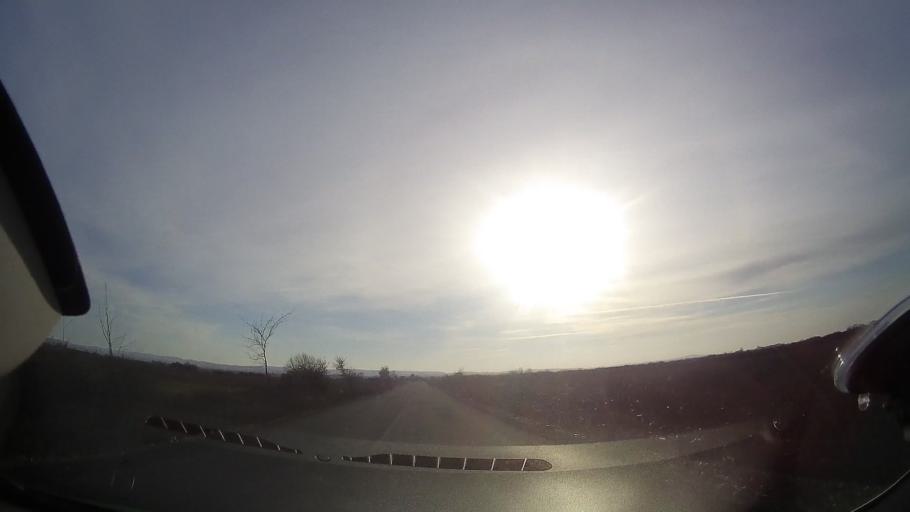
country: RO
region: Bihor
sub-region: Comuna Tileagd
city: Tileagd
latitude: 47.0891
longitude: 22.1771
